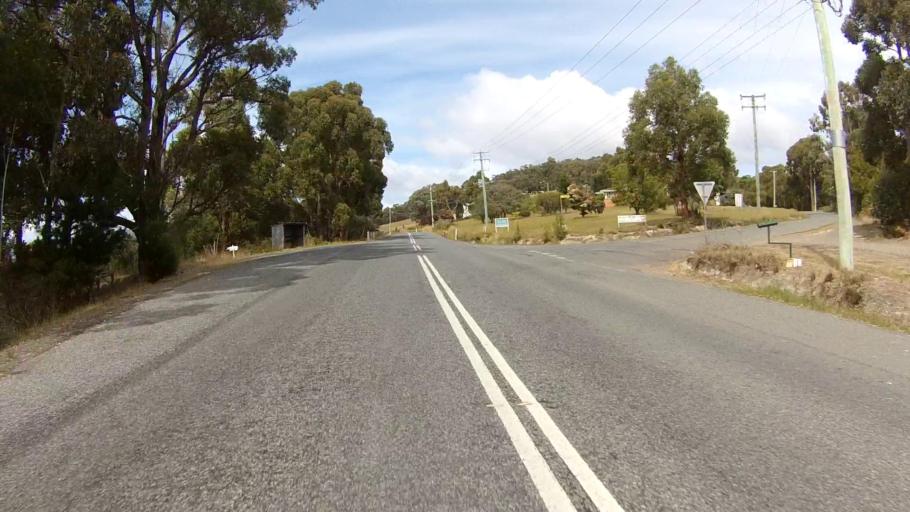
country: AU
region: Tasmania
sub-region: Kingborough
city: Kettering
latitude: -43.1387
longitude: 147.2450
